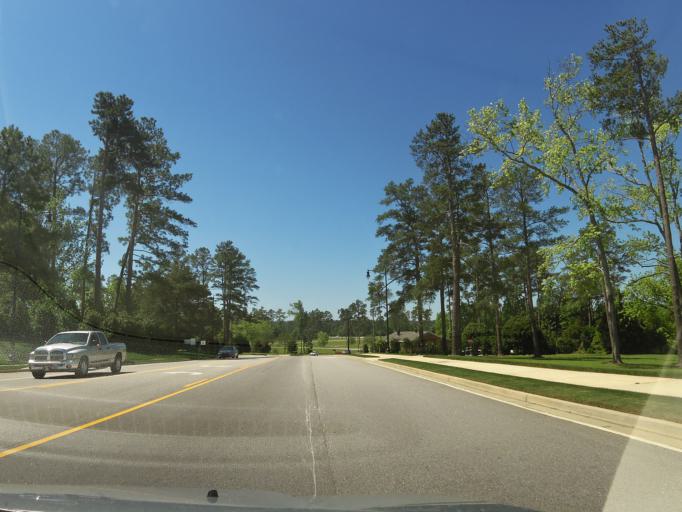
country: US
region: Georgia
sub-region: Columbia County
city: Martinez
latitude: 33.5087
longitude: -82.0290
